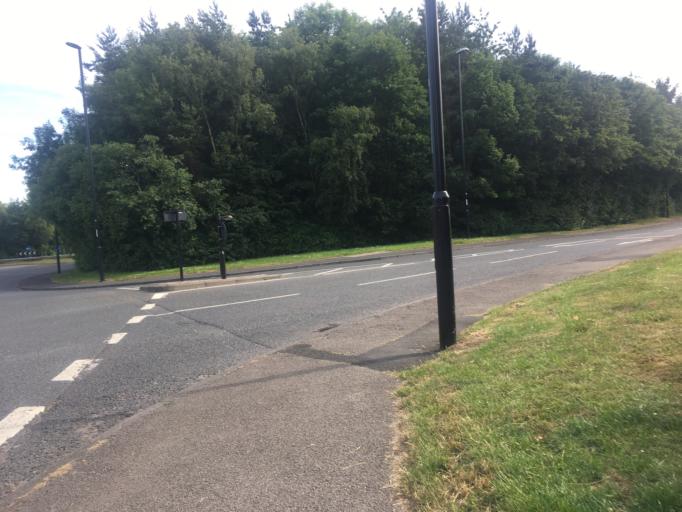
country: GB
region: England
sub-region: Sunderland
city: Washington
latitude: 54.8891
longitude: -1.5405
